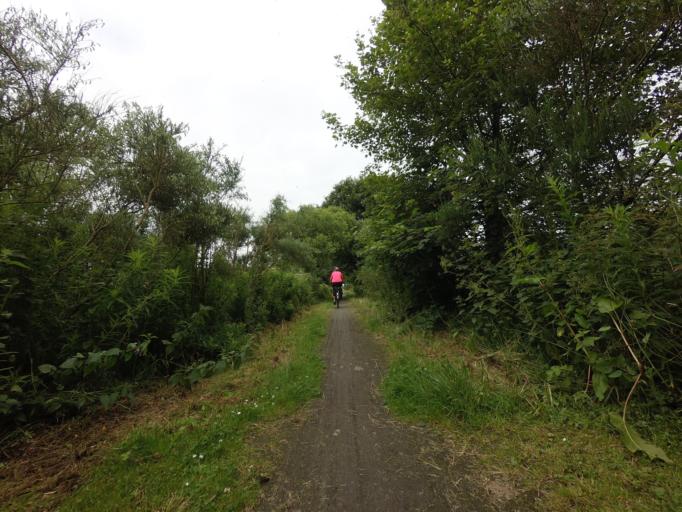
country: GB
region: Scotland
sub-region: Aberdeenshire
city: Ellon
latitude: 57.4673
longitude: -2.1179
